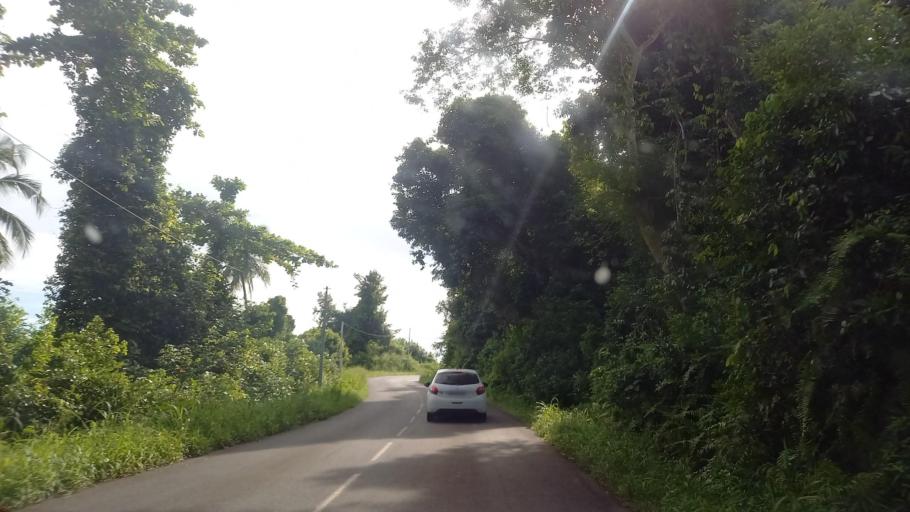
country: YT
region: Ouangani
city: Ouangani
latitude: -12.8840
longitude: 45.1310
